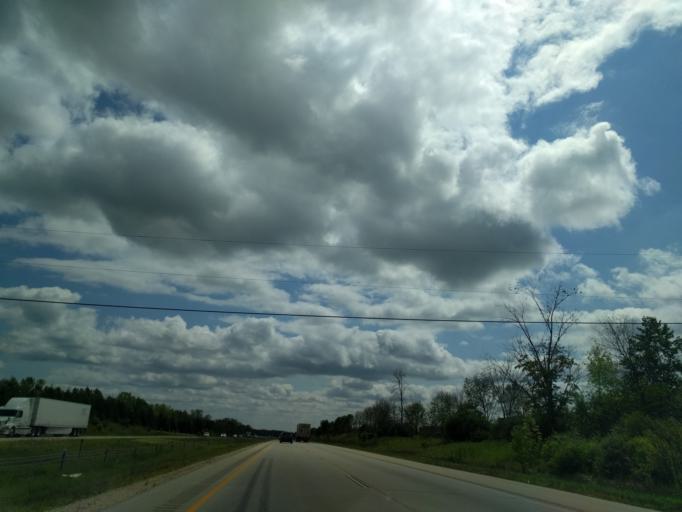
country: US
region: Wisconsin
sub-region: Ozaukee County
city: Thiensville
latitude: 43.2435
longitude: -87.9200
